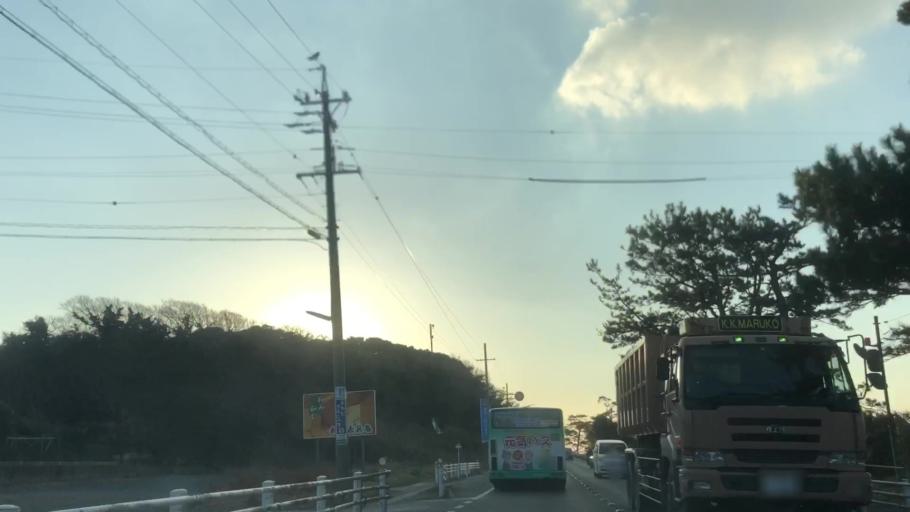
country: JP
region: Aichi
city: Tahara
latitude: 34.6591
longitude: 137.1766
